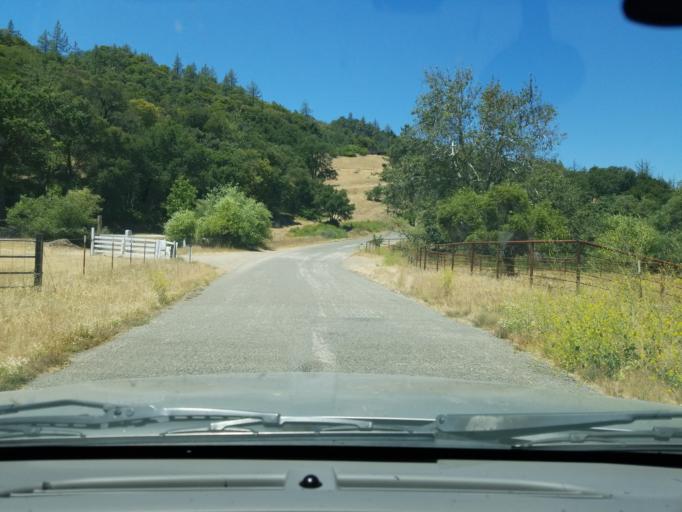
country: US
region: California
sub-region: Monterey County
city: Gonzales
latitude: 36.3378
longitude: -121.5348
